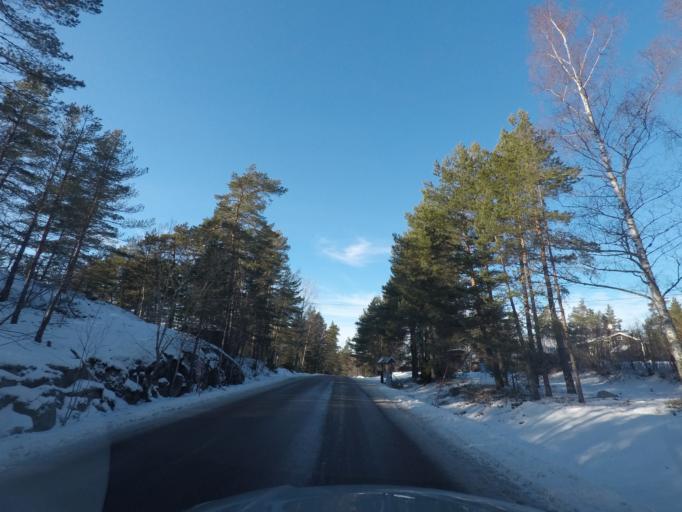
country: SE
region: Soedermanland
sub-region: Eskilstuna Kommun
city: Hallbybrunn
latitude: 59.4261
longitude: 16.4287
